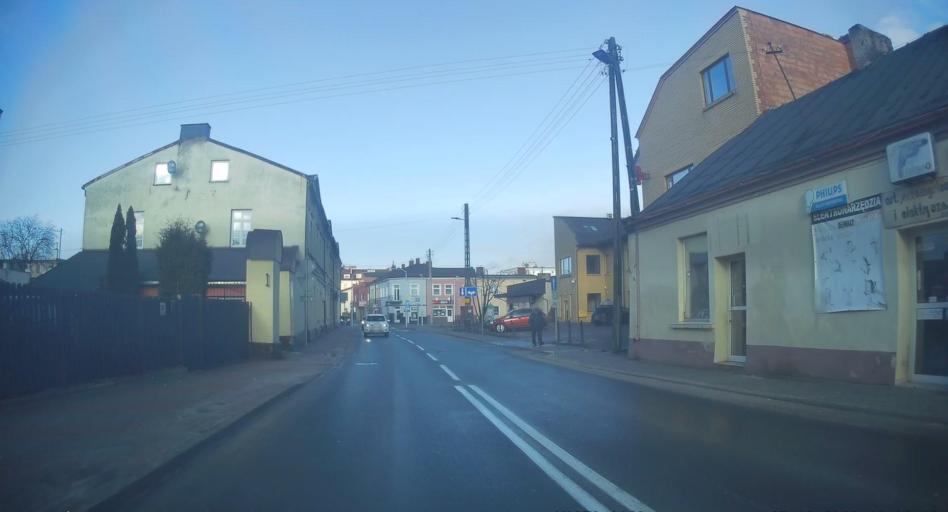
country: PL
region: Lodz Voivodeship
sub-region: Powiat rawski
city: Rawa Mazowiecka
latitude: 51.7638
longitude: 20.2548
